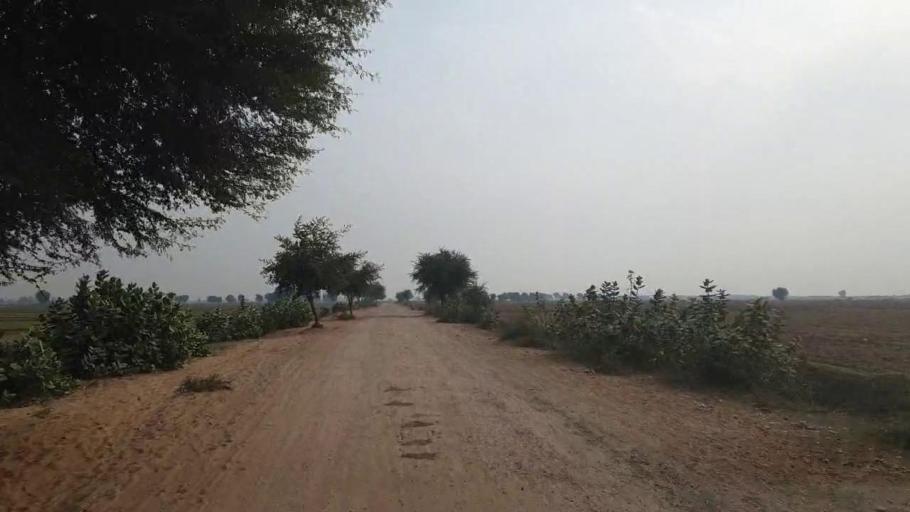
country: PK
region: Sindh
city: Sann
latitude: 26.0269
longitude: 68.1405
